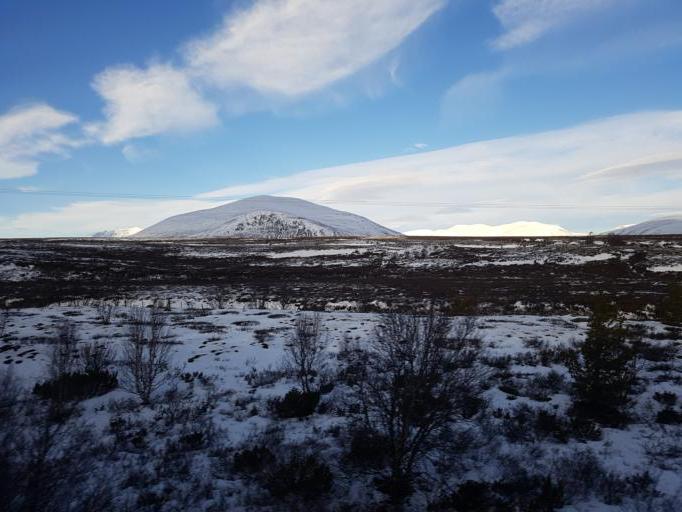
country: NO
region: Sor-Trondelag
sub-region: Oppdal
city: Oppdal
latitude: 62.2721
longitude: 9.5841
